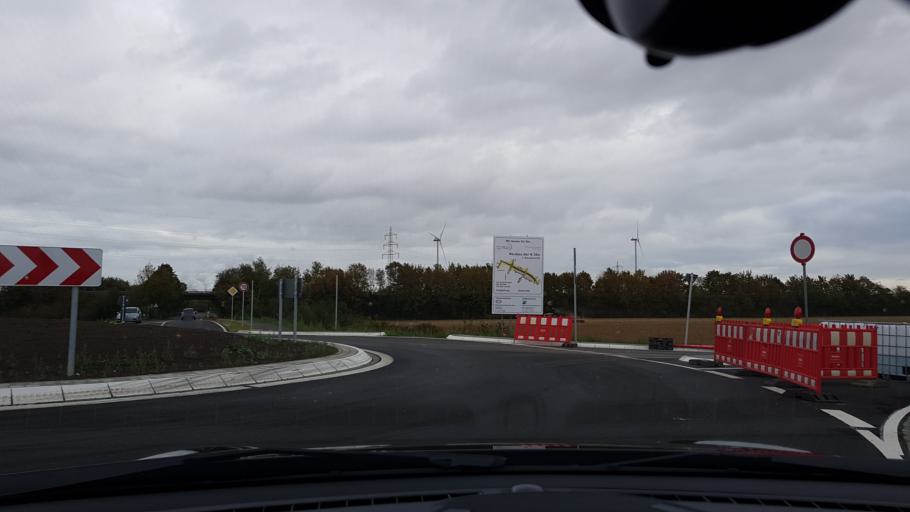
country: DE
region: North Rhine-Westphalia
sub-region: Regierungsbezirk Koln
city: Elsdorf
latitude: 50.9473
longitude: 6.5690
